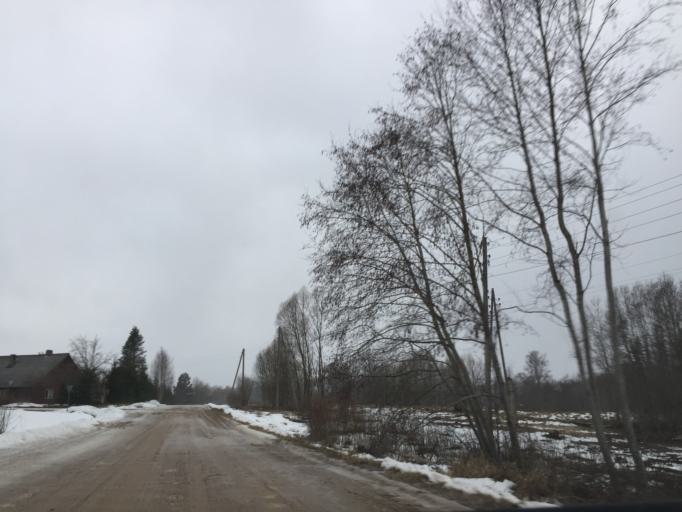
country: LV
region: Salacgrivas
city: Salacgriva
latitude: 57.6495
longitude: 24.4729
